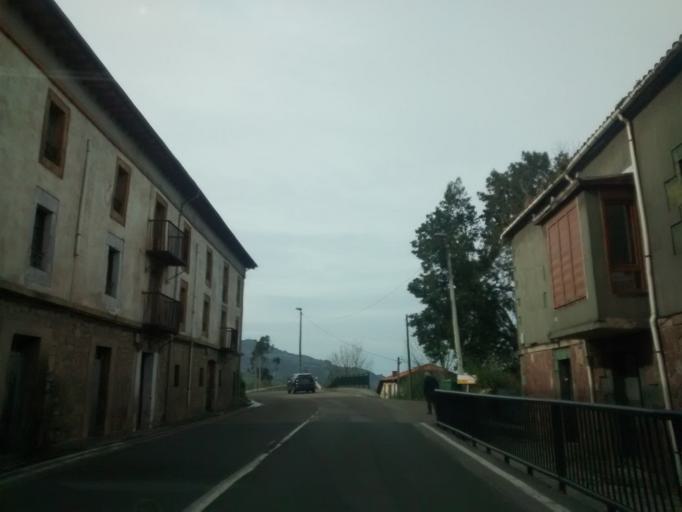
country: ES
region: Cantabria
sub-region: Provincia de Cantabria
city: Santiurde de Toranzo
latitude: 43.2014
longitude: -3.9291
